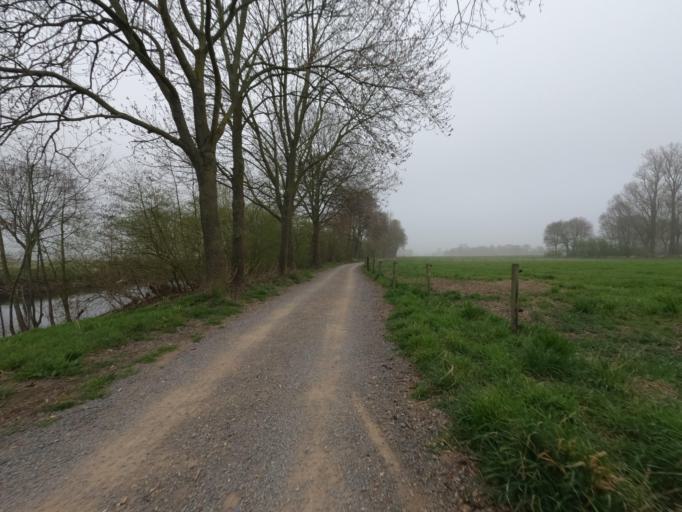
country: DE
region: North Rhine-Westphalia
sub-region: Regierungsbezirk Koln
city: Heinsberg
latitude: 51.0986
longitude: 6.1017
